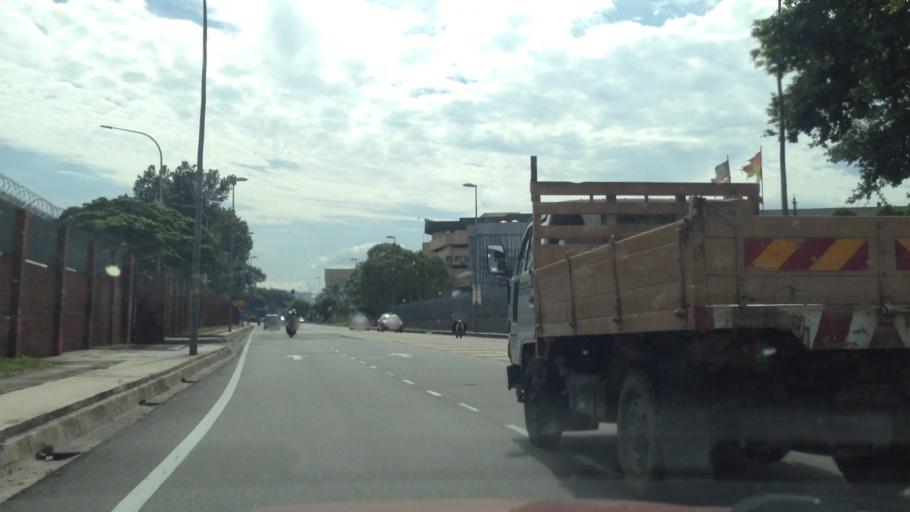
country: MY
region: Selangor
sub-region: Petaling
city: Petaling Jaya
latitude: 3.0824
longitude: 101.6206
